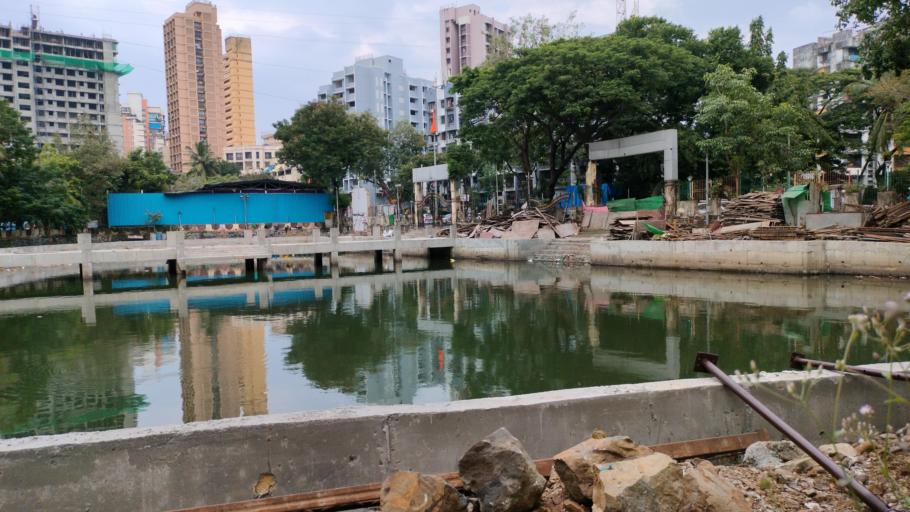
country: IN
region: Maharashtra
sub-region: Mumbai Suburban
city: Borivli
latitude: 19.1813
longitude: 72.8377
